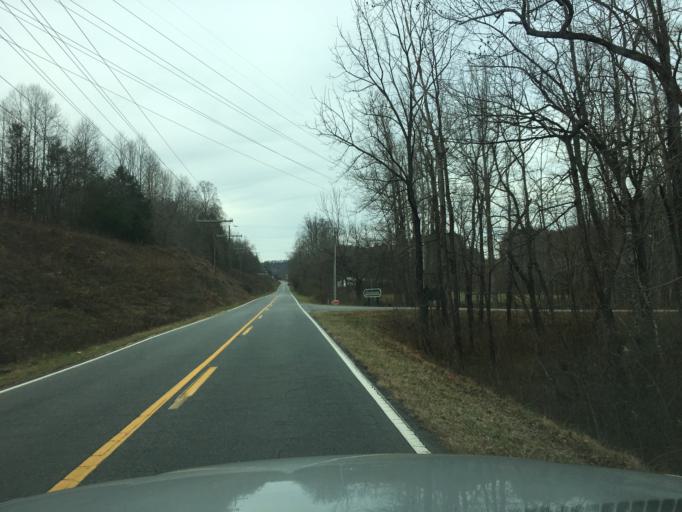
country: US
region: North Carolina
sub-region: McDowell County
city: West Marion
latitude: 35.6307
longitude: -81.9828
